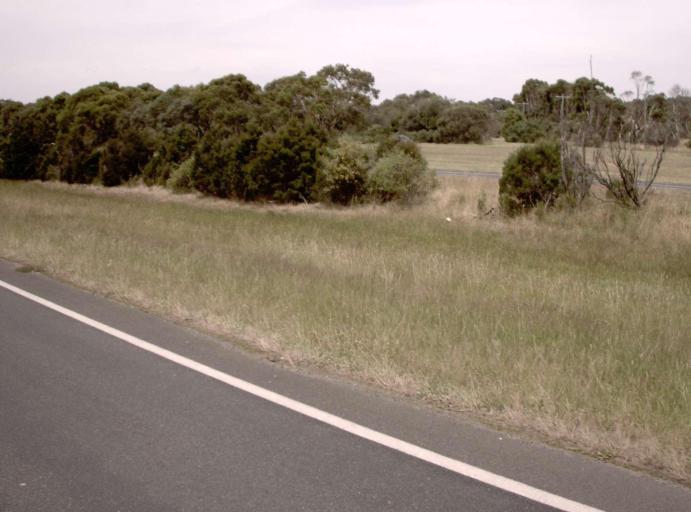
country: AU
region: Victoria
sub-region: Mornington Peninsula
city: Safety Beach
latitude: -38.3039
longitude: 145.0266
